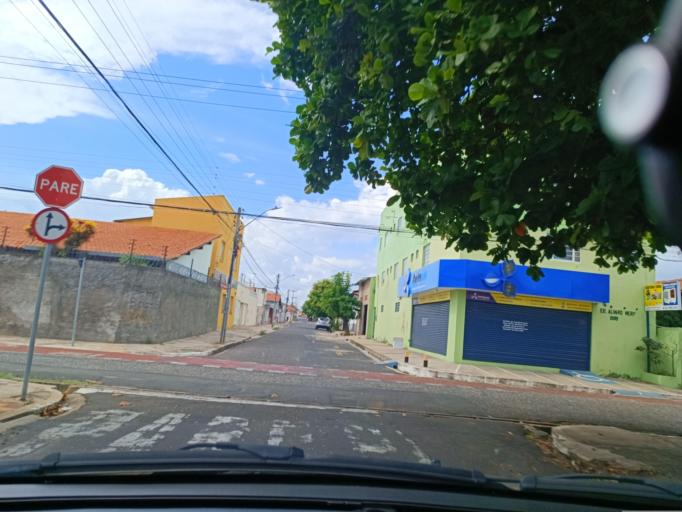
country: BR
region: Piaui
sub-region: Teresina
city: Teresina
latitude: -5.0831
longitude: -42.8153
